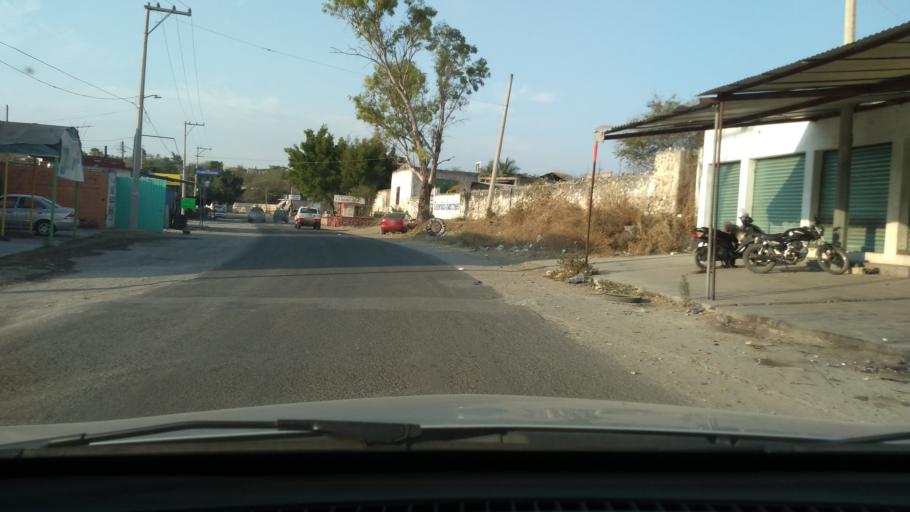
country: MX
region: Morelos
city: Puente de Ixtla
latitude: 18.6124
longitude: -99.3123
